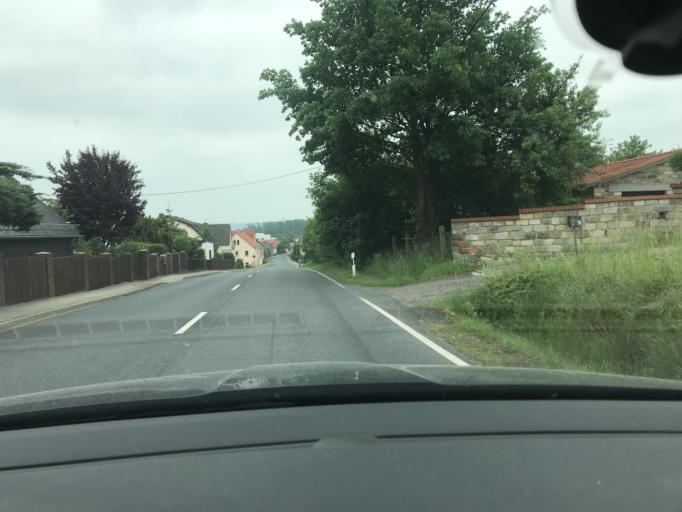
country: DE
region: Saxony
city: Niederau
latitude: 51.1976
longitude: 13.5064
